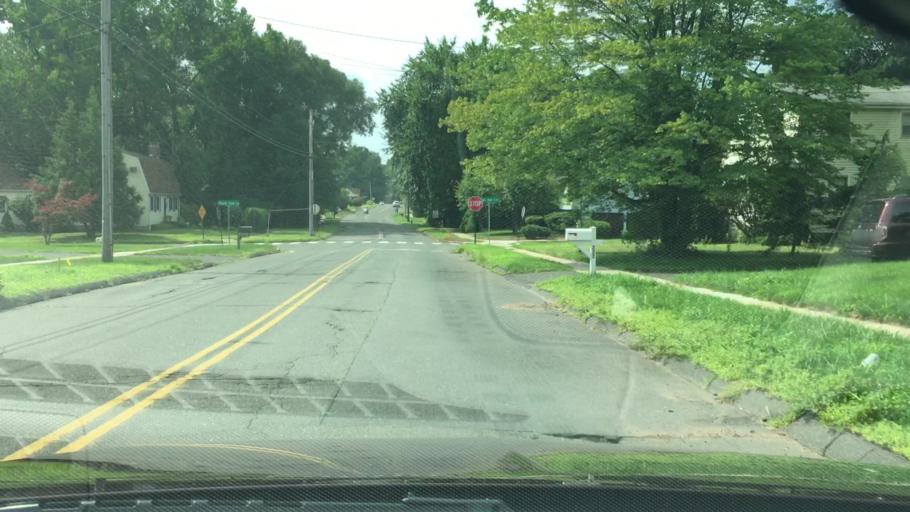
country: US
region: Connecticut
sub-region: Hartford County
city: Kensington
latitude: 41.6251
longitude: -72.7671
